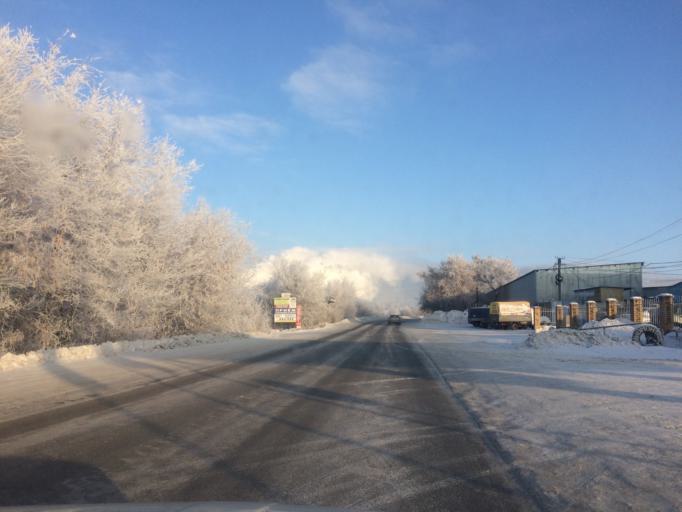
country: RU
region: Chelyabinsk
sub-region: Gorod Magnitogorsk
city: Magnitogorsk
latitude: 53.3982
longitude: 59.0868
